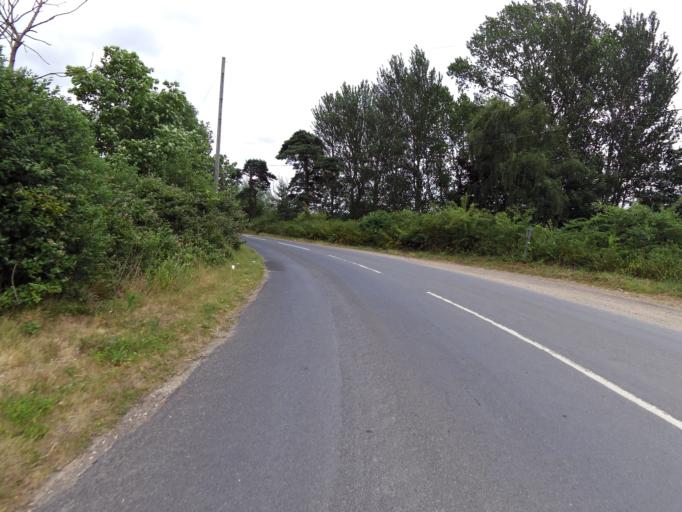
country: GB
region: England
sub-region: Suffolk
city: Bungay
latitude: 52.4416
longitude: 1.3980
